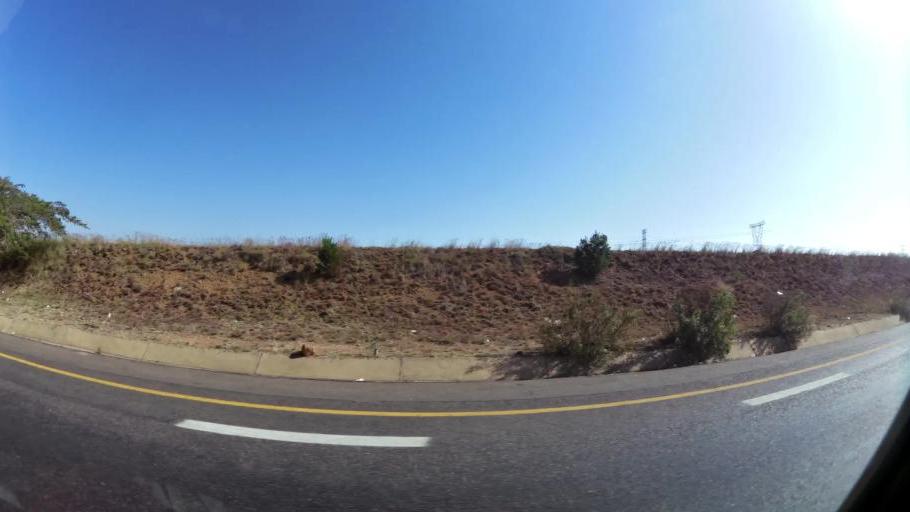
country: ZA
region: Gauteng
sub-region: City of Tshwane Metropolitan Municipality
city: Mabopane
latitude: -25.5502
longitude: 28.1094
